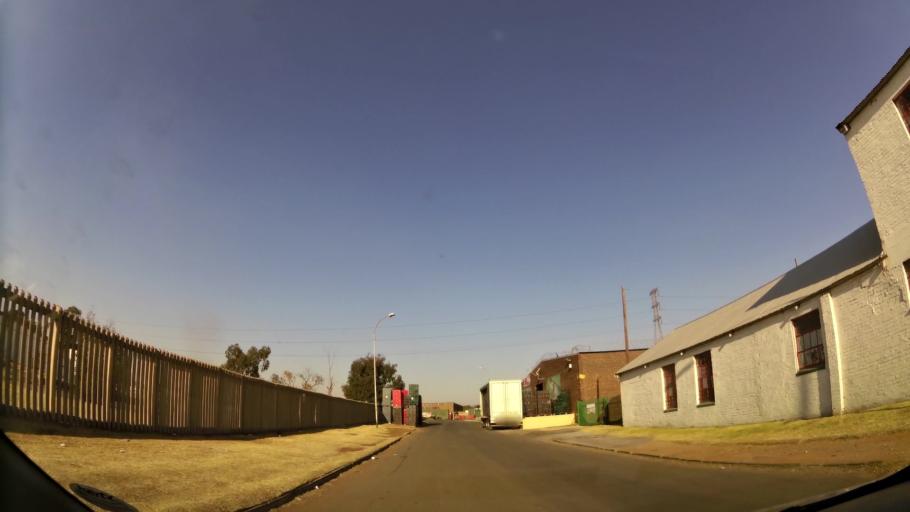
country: ZA
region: Gauteng
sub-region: West Rand District Municipality
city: Randfontein
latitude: -26.1907
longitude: 27.6928
